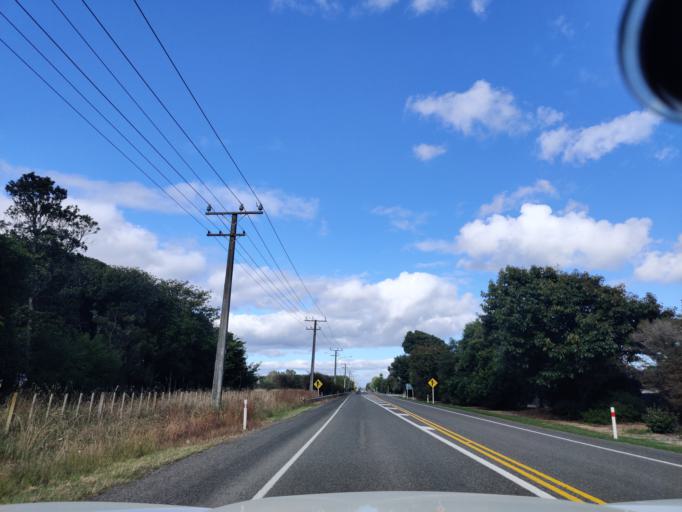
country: NZ
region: Manawatu-Wanganui
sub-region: Horowhenua District
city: Levin
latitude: -40.6325
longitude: 175.3043
